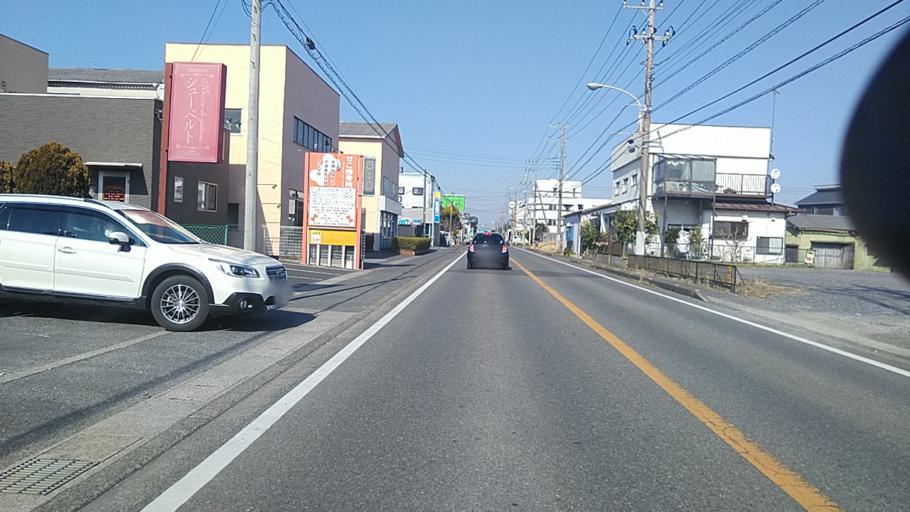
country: JP
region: Chiba
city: Mobara
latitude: 35.4432
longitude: 140.2954
